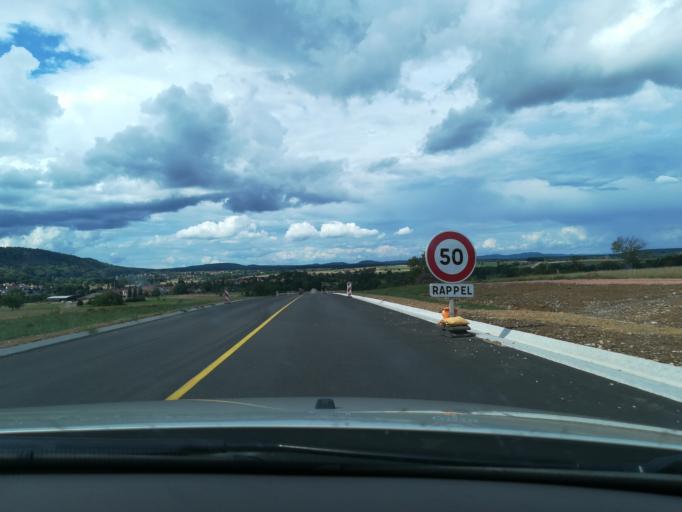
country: FR
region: Alsace
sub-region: Departement du Bas-Rhin
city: Dossenheim-sur-Zinsel
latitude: 48.7950
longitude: 7.4030
